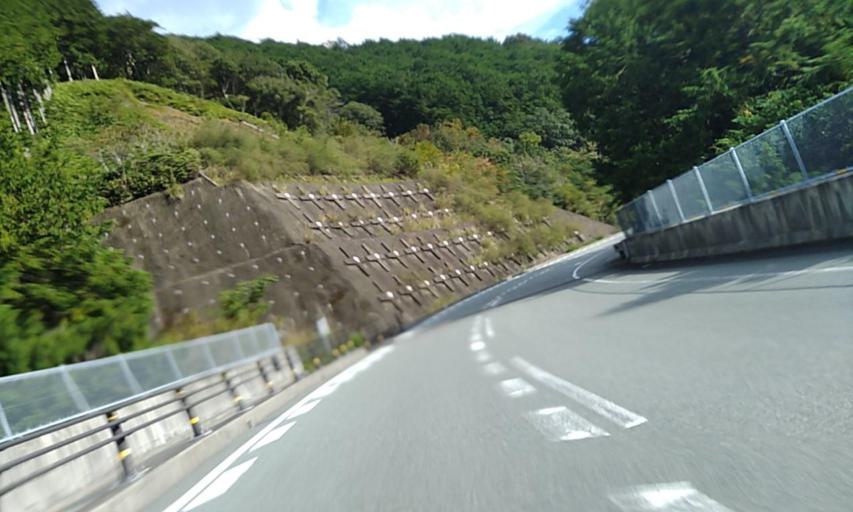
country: JP
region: Mie
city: Owase
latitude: 34.2528
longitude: 136.4297
